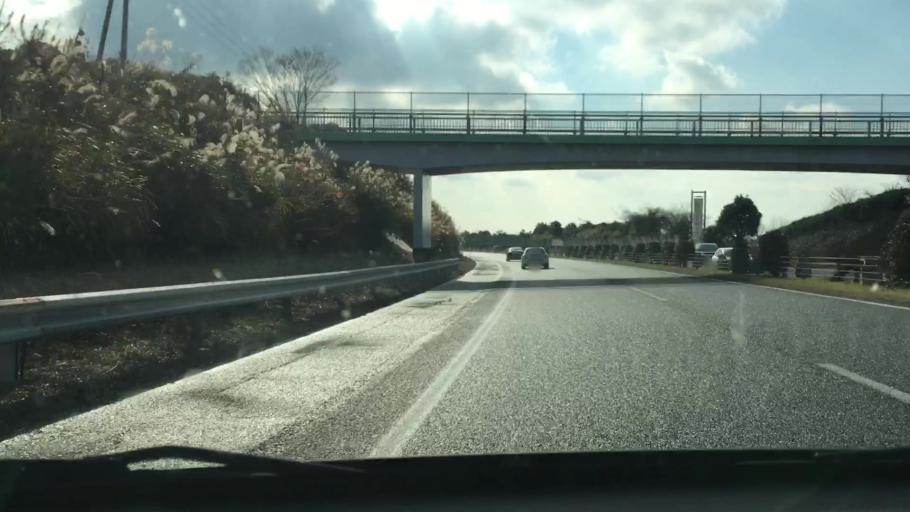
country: JP
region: Kumamoto
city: Yatsushiro
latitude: 32.5390
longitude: 130.6752
